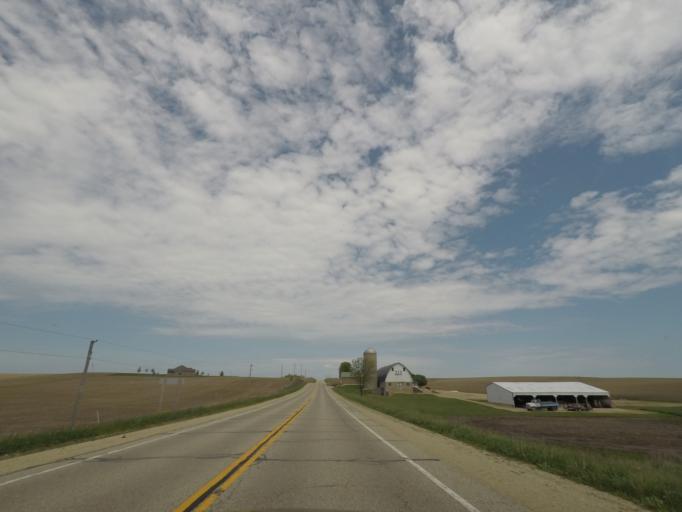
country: US
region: Wisconsin
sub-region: Rock County
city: Orfordville
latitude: 42.6881
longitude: -89.2882
